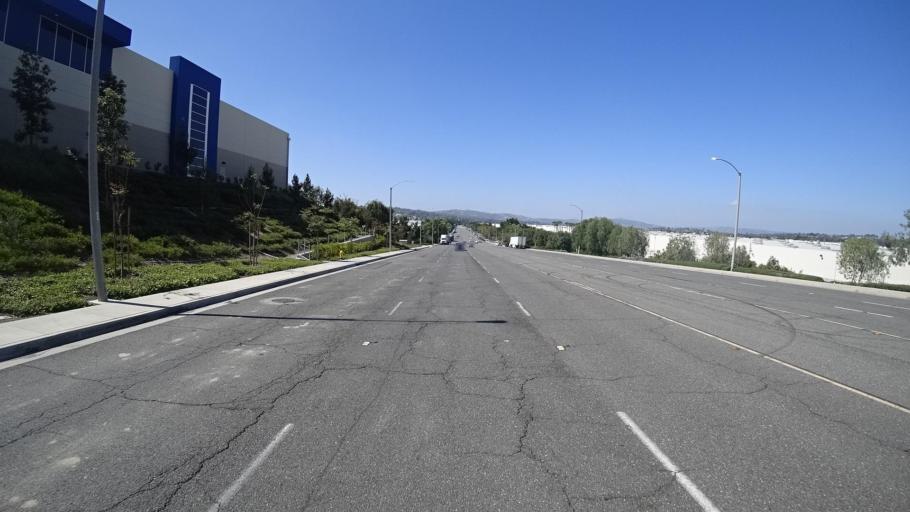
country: US
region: California
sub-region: Los Angeles County
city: Diamond Bar
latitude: 34.0192
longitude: -117.8296
